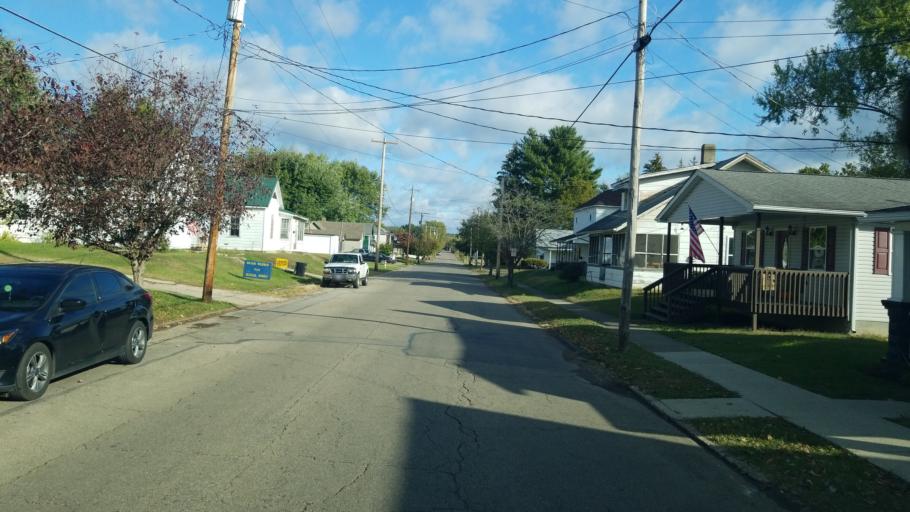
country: US
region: Ohio
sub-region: Jackson County
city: Wellston
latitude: 39.1168
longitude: -82.5390
